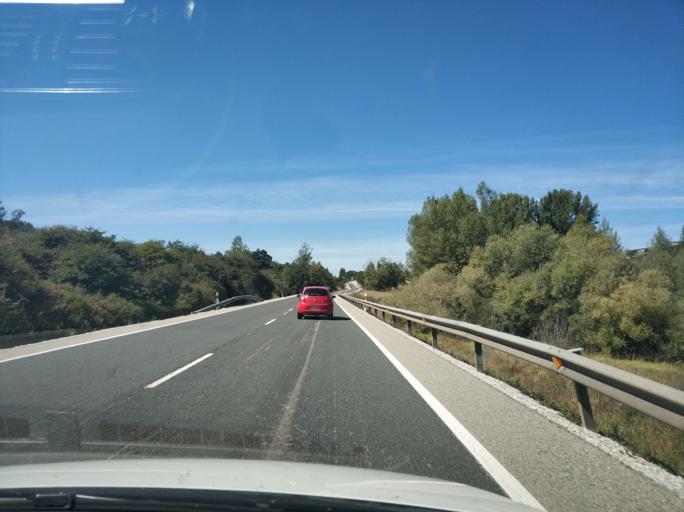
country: ES
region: Castille and Leon
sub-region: Provincia de Burgos
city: Basconcillos del Tozo
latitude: 42.7167
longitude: -4.0233
